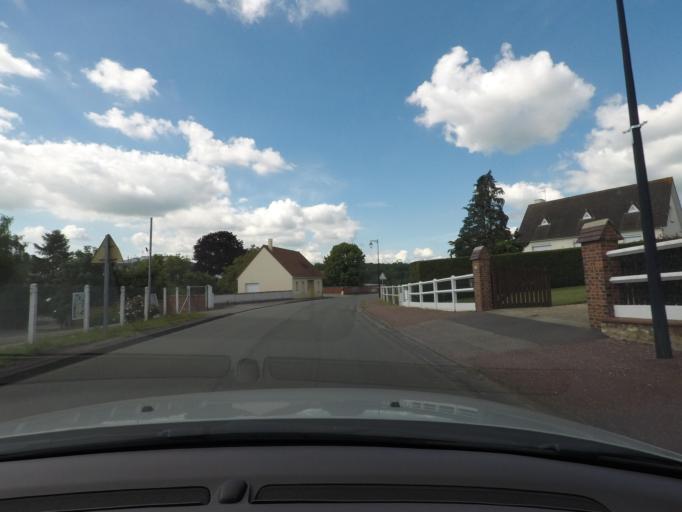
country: FR
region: Haute-Normandie
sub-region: Departement de l'Eure
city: Damville
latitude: 48.8701
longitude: 1.0792
